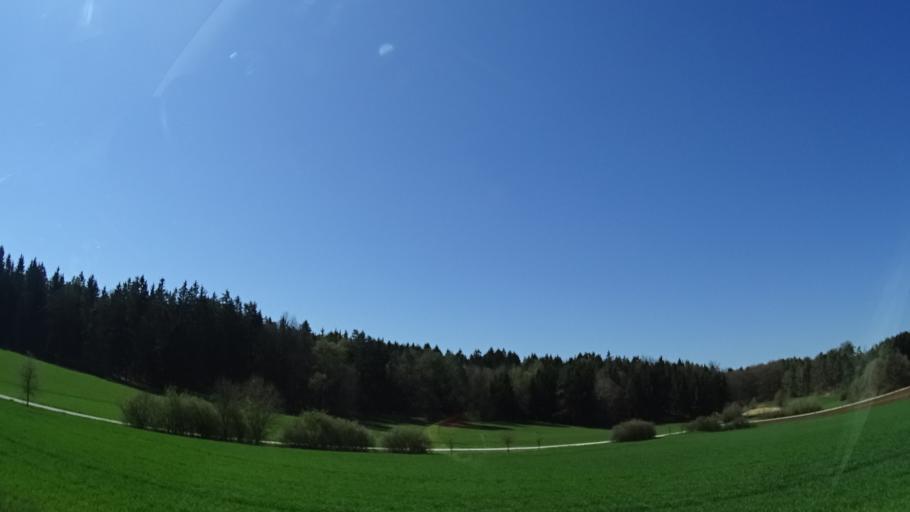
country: DE
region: Bavaria
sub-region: Upper Palatinate
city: Illschwang
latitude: 49.4107
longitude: 11.6450
